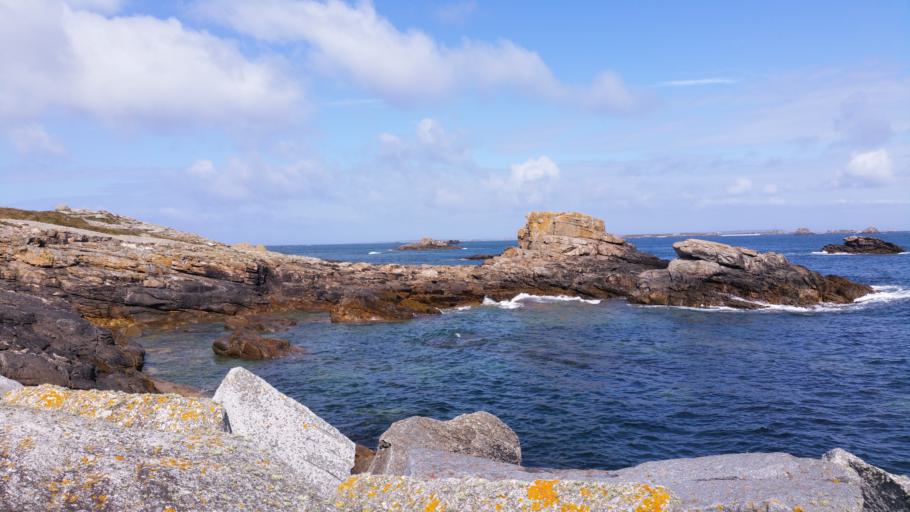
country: FR
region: Brittany
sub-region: Departement du Finistere
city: Le Conquet
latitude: 48.4013
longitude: -4.9586
